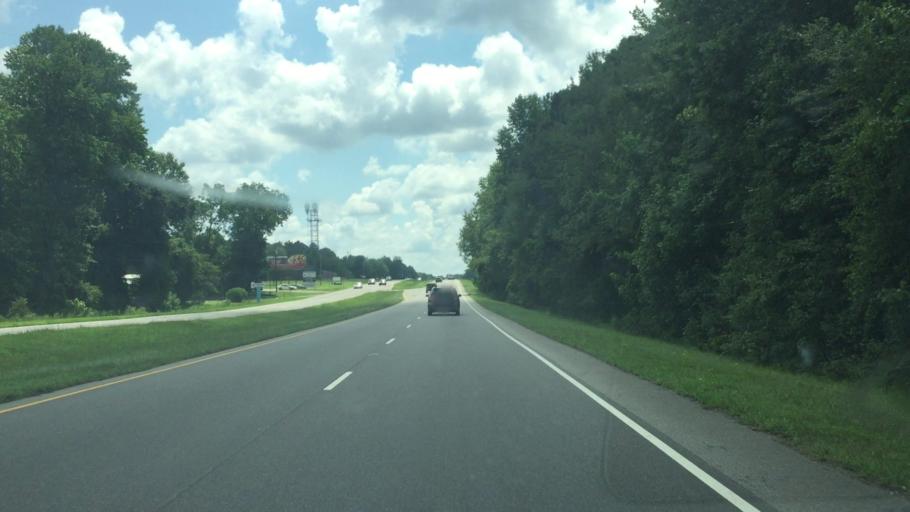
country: US
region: North Carolina
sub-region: Scotland County
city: Laurel Hill
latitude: 34.7971
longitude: -79.5182
